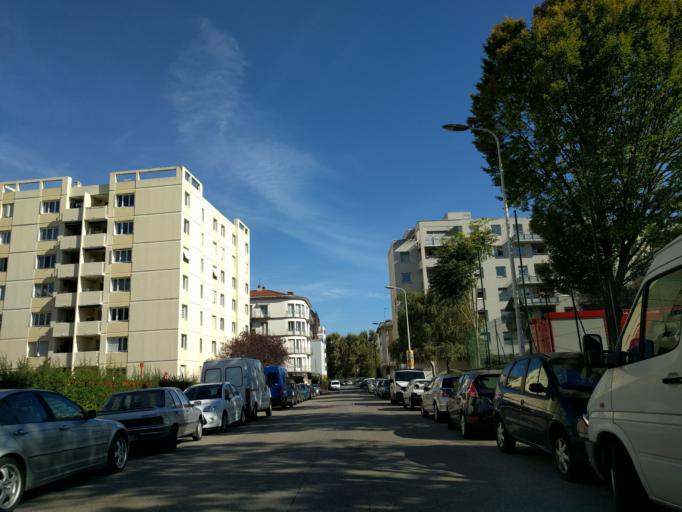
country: FR
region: Rhone-Alpes
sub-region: Departement du Rhone
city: La Mulatiere
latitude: 45.7328
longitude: 4.8287
